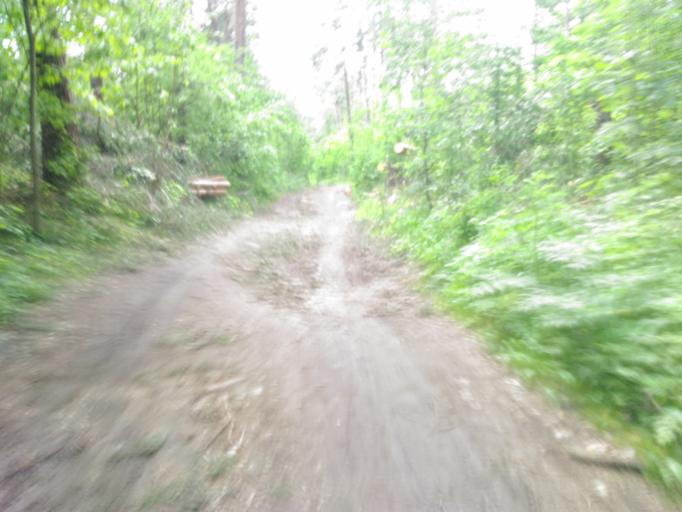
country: RU
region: Moscow
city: Rublevo
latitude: 55.7684
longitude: 37.3540
